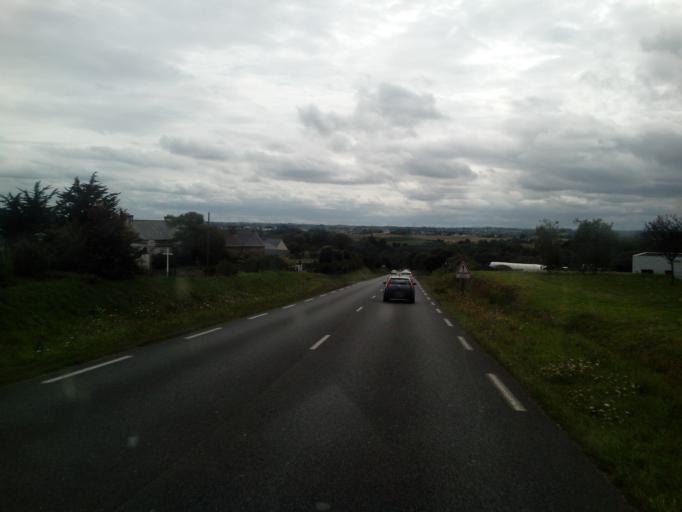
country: FR
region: Brittany
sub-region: Departement des Cotes-d'Armor
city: Binic
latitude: 48.6092
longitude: -2.8338
